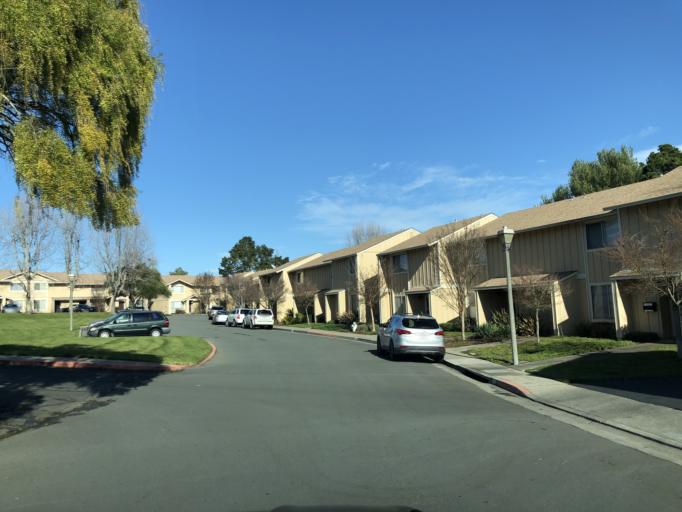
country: US
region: California
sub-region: Contra Costa County
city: Tara Hills
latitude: 37.9826
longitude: -122.3087
